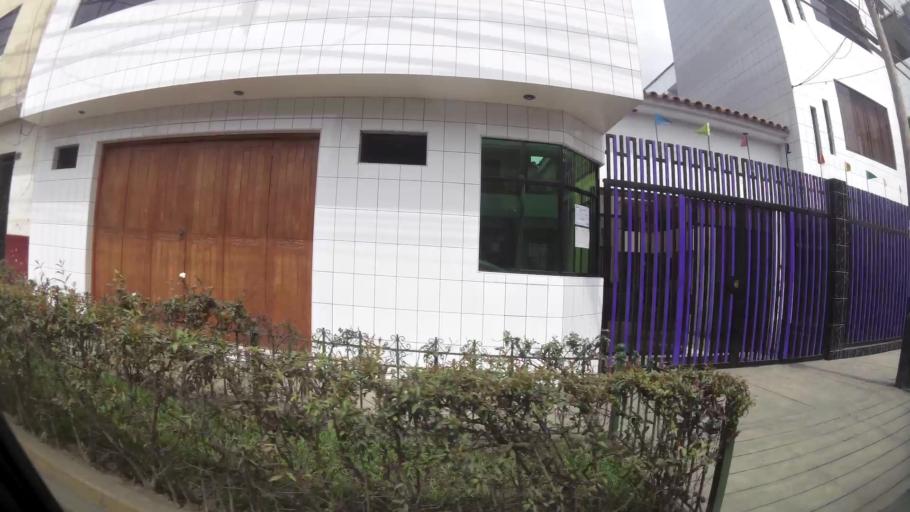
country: PE
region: Lima
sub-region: Provincia de Huaral
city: Huaral
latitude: -11.4959
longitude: -77.2145
